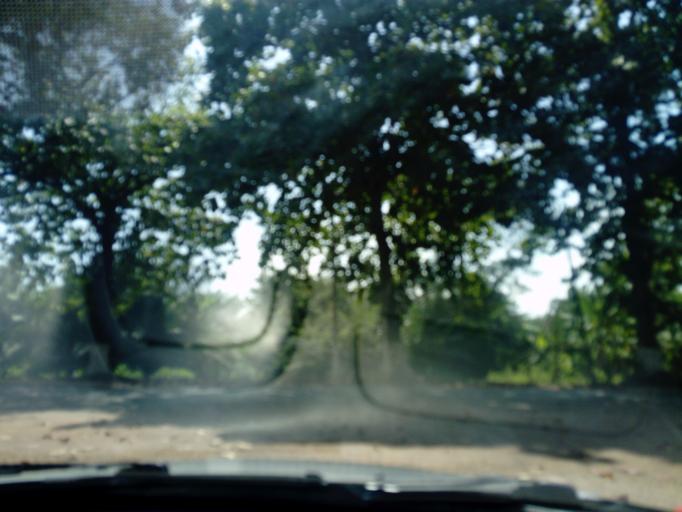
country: GH
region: Central
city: Cape Coast
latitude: 5.1121
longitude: -1.2879
